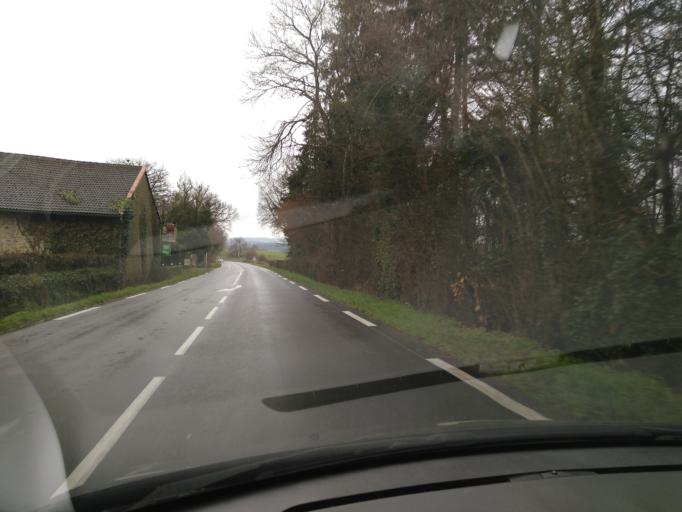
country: FR
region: Limousin
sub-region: Departement de la Haute-Vienne
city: Condat-sur-Vienne
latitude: 45.7702
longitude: 1.2900
